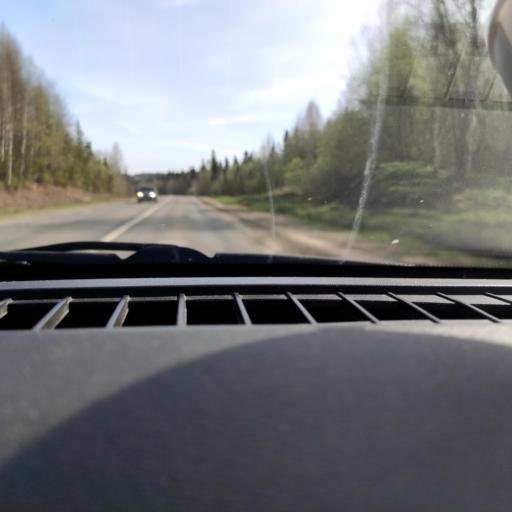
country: RU
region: Perm
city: Perm
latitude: 58.2424
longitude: 56.1583
